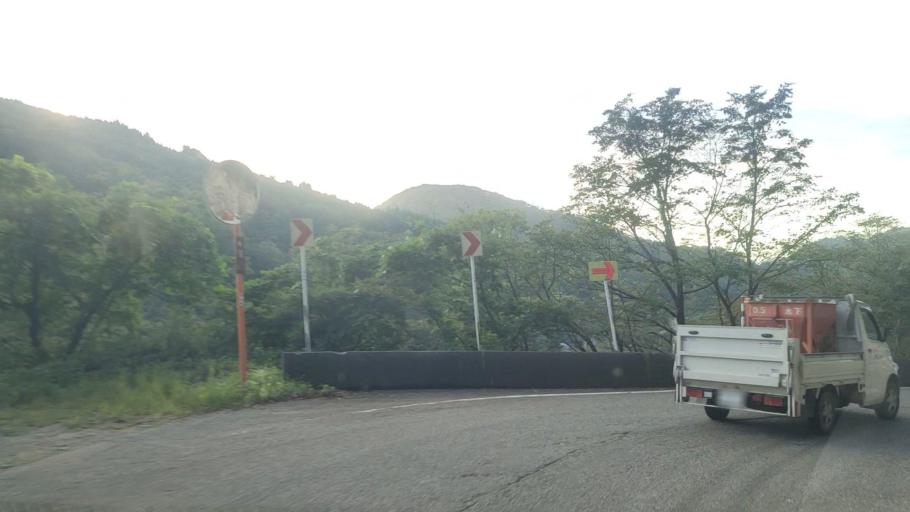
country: JP
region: Toyama
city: Nanto-shi
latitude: 36.5537
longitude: 137.0116
